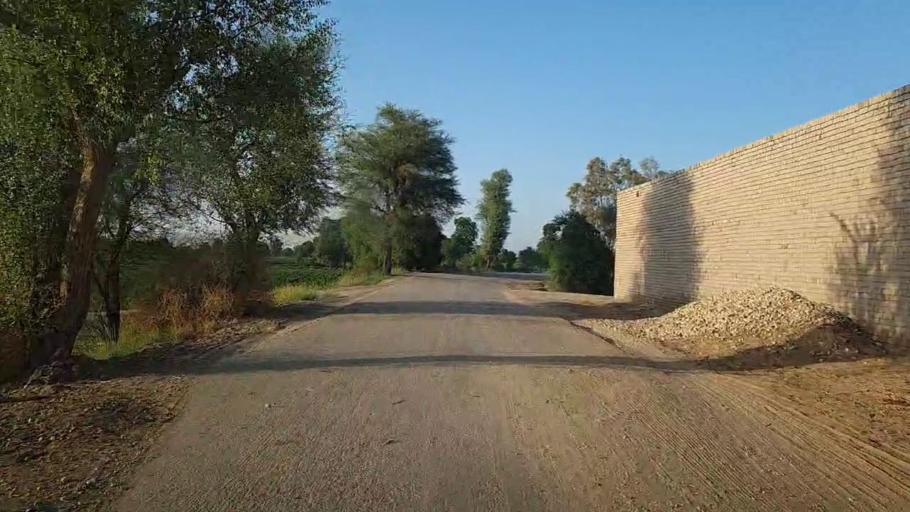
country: PK
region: Sindh
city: Bhan
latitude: 26.5816
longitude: 67.7607
